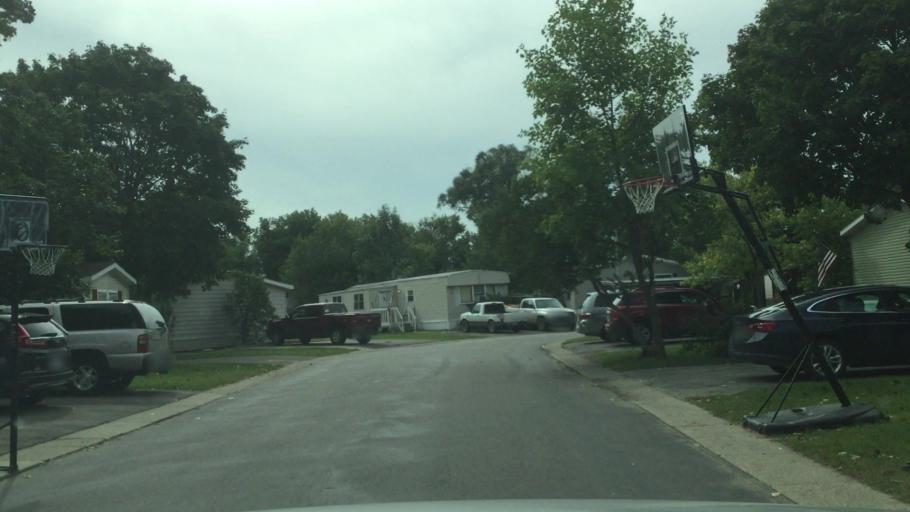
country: US
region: Michigan
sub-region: Oakland County
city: Holly
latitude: 42.8088
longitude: -83.6241
